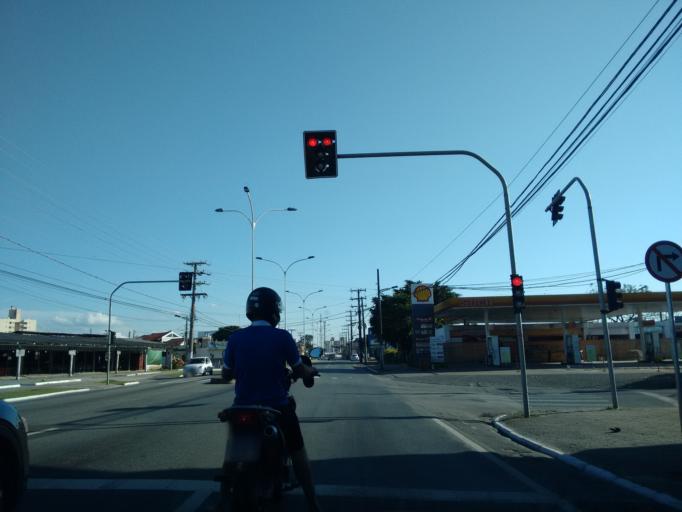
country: BR
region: Santa Catarina
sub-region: Itajai
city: Itajai
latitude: -26.8843
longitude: -48.6953
